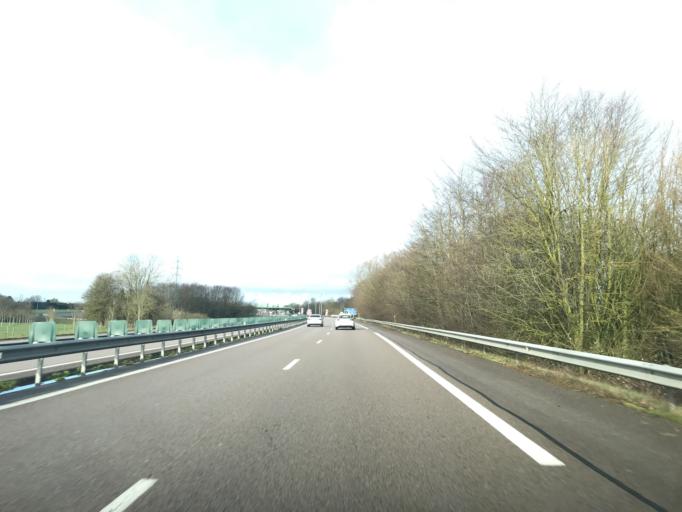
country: FR
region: Haute-Normandie
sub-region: Departement de l'Eure
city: Beuzeville
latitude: 49.3380
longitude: 0.3736
